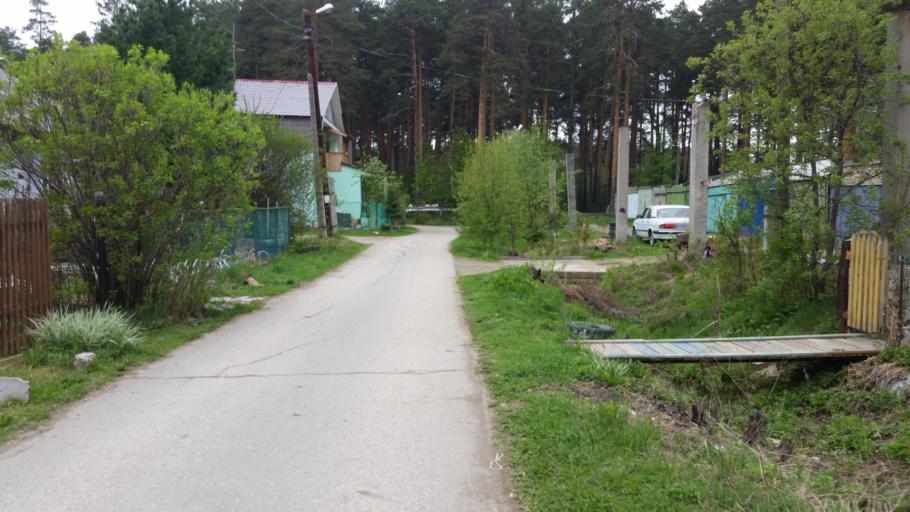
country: RU
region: Sverdlovsk
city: Beryozovsky
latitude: 56.9022
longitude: 60.7652
